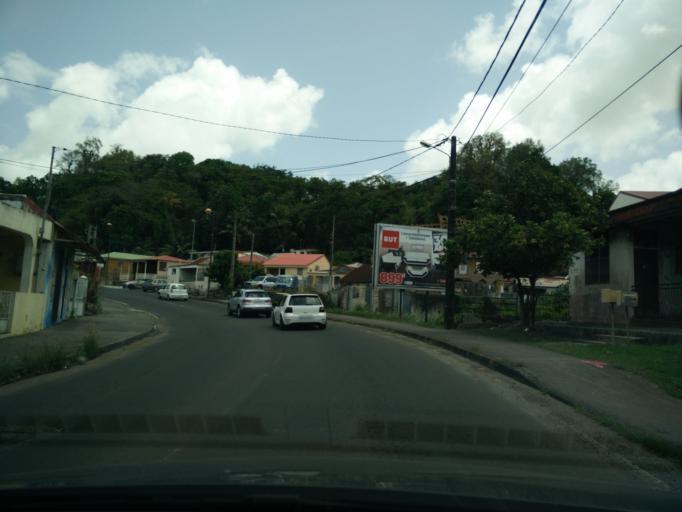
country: GP
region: Guadeloupe
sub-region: Guadeloupe
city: Les Abymes
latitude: 16.2737
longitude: -61.5049
